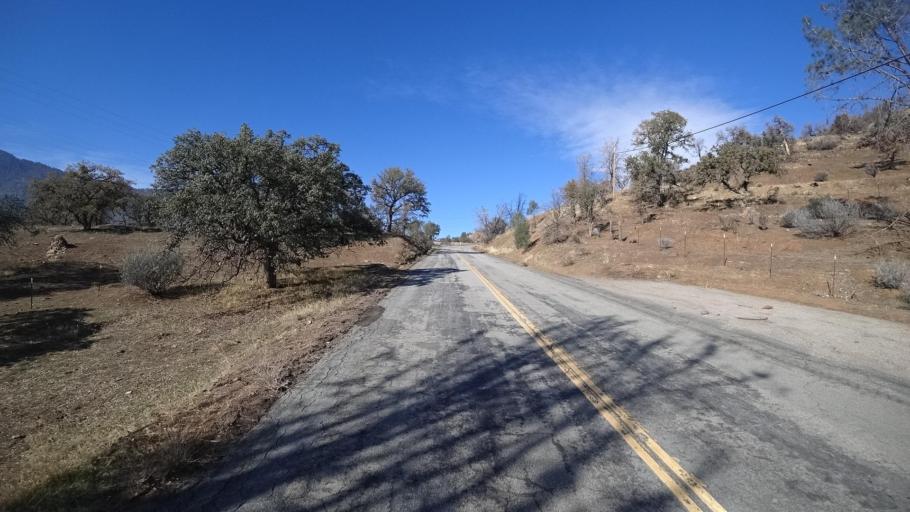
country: US
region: California
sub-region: Kern County
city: Bodfish
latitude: 35.4473
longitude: -118.5290
